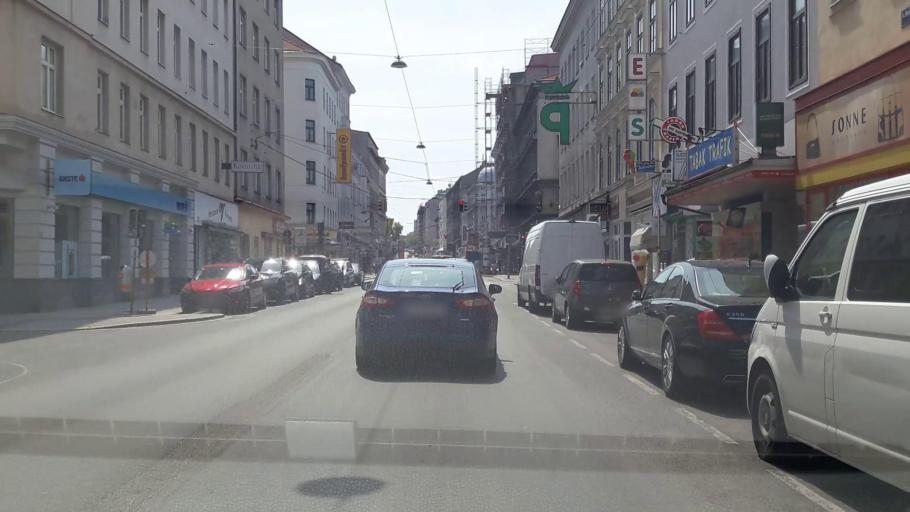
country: AT
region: Vienna
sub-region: Wien Stadt
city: Vienna
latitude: 48.1870
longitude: 16.3528
